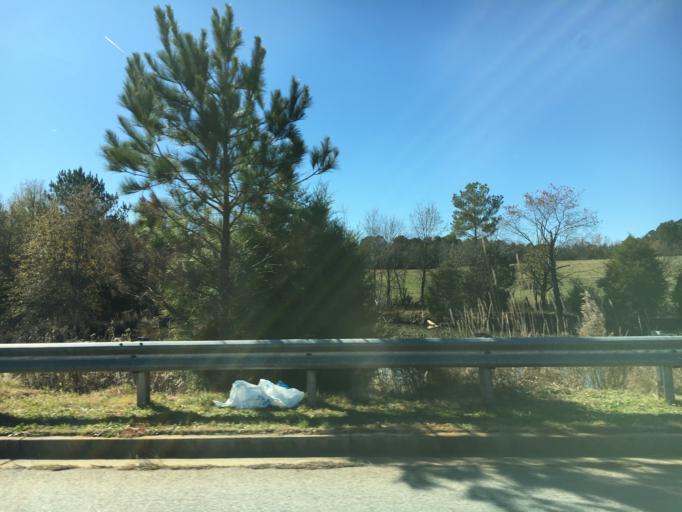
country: US
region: South Carolina
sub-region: Spartanburg County
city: Roebuck
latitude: 34.8724
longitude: -82.0356
